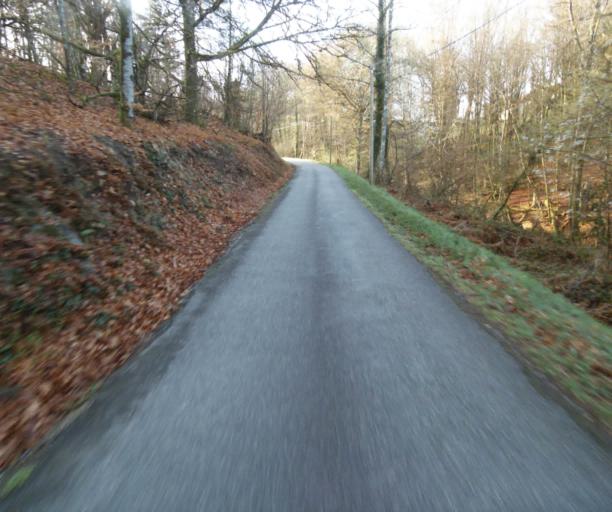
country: FR
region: Limousin
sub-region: Departement de la Correze
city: Correze
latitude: 45.2943
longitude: 1.8483
